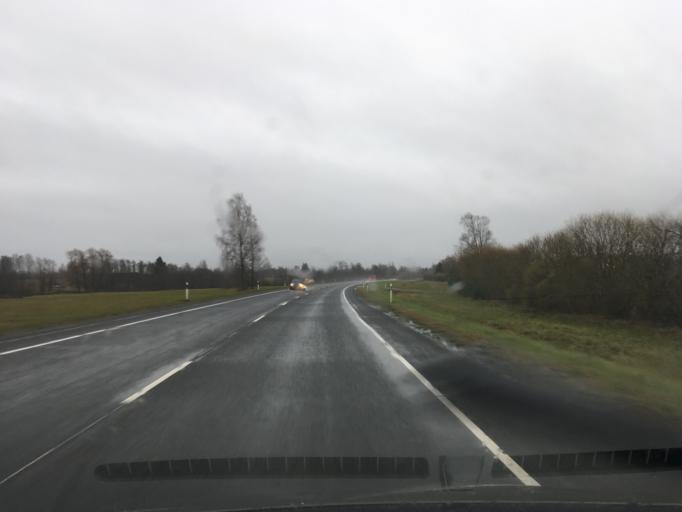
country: EE
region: Harju
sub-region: Nissi vald
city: Turba
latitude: 58.9236
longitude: 24.1117
